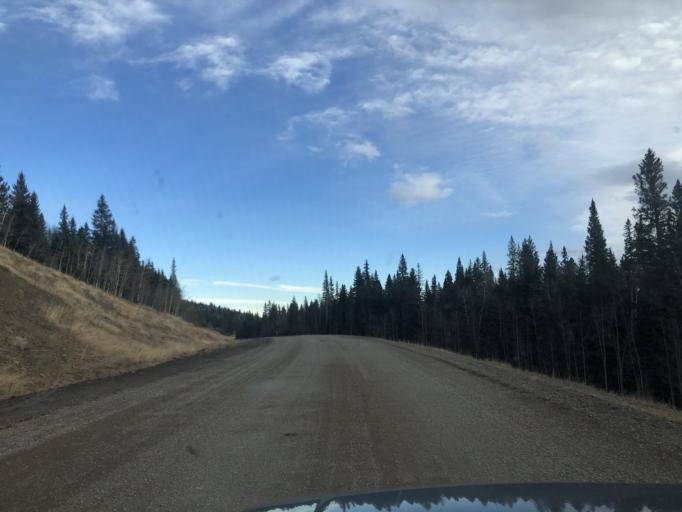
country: CA
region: Alberta
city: Cochrane
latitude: 51.0418
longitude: -114.7484
